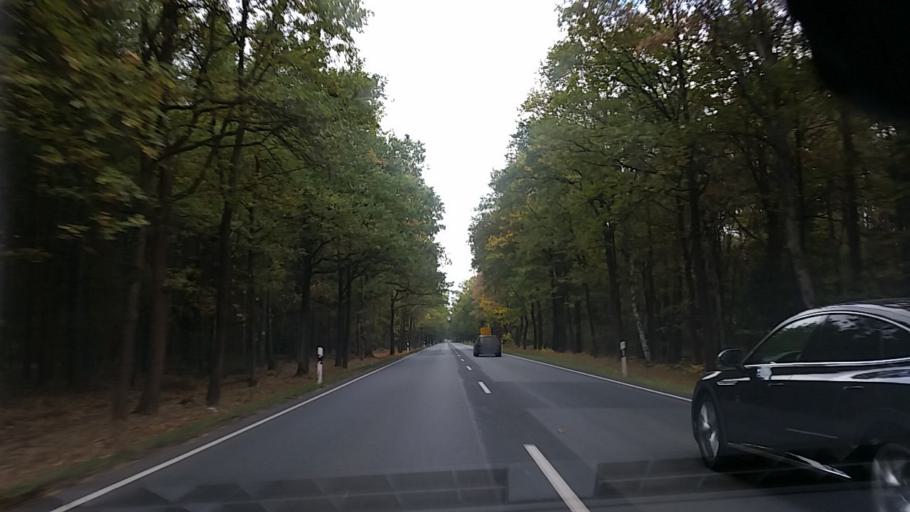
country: DE
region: Lower Saxony
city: Dedelstorf
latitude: 52.7290
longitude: 10.4845
